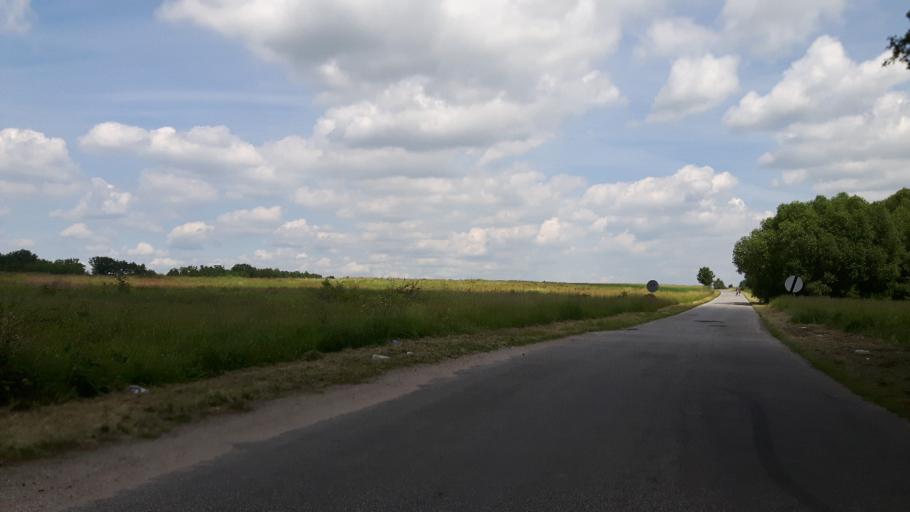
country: PL
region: West Pomeranian Voivodeship
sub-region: Powiat goleniowski
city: Osina
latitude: 53.6446
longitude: 14.9361
